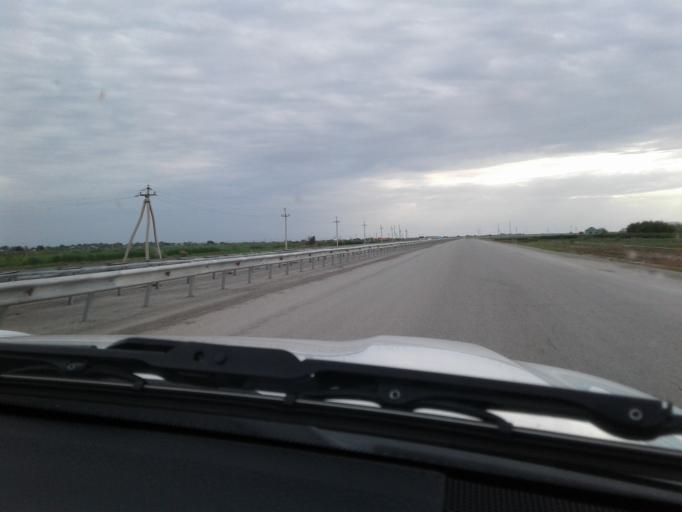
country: TM
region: Ahal
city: Tejen
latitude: 37.3430
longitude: 60.5895
